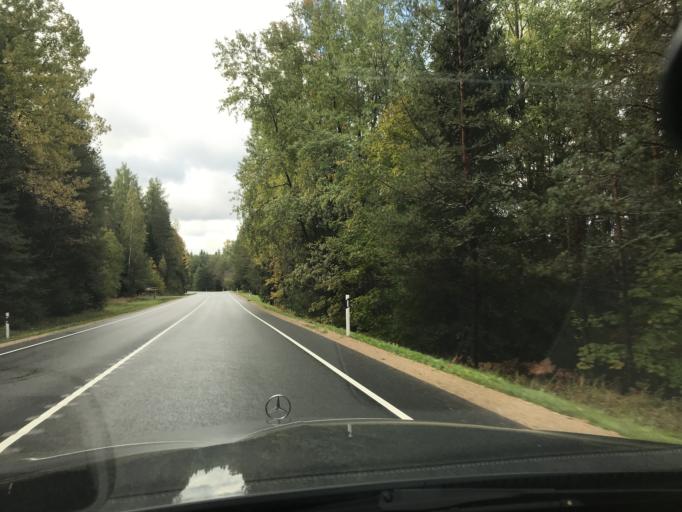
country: EE
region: Viljandimaa
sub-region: Karksi vald
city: Karksi-Nuia
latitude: 58.0410
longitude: 25.6459
